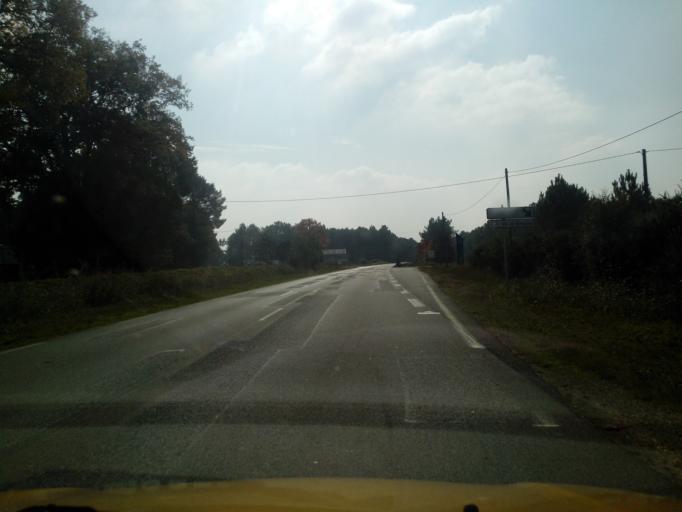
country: FR
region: Brittany
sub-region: Departement du Morbihan
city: Molac
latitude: 47.7451
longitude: -2.4372
